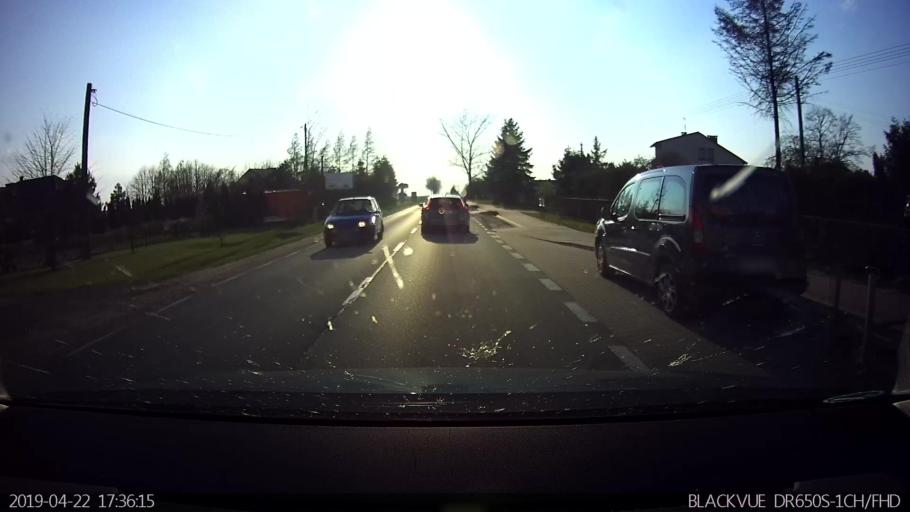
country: PL
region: Masovian Voivodeship
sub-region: Powiat sokolowski
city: Sokolow Podlaski
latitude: 52.4075
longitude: 22.1920
